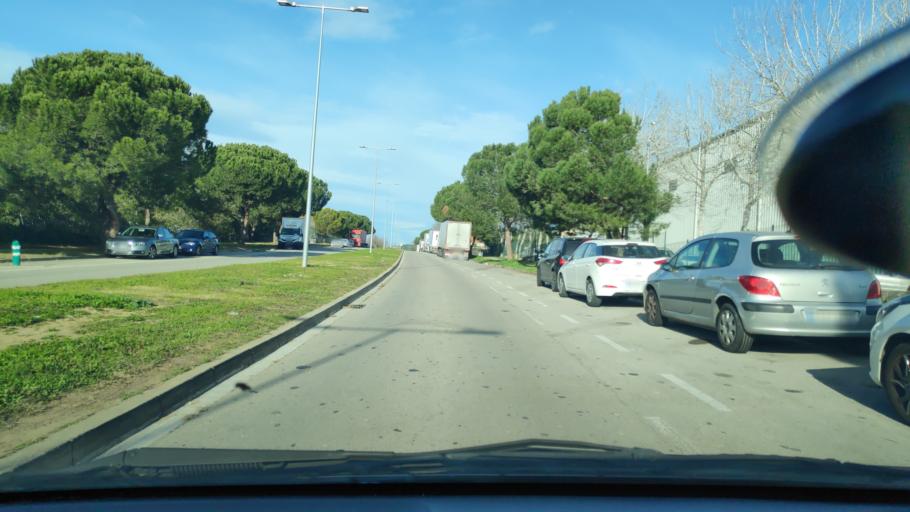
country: ES
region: Catalonia
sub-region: Provincia de Barcelona
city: Rubi
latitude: 41.4870
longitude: 2.0470
